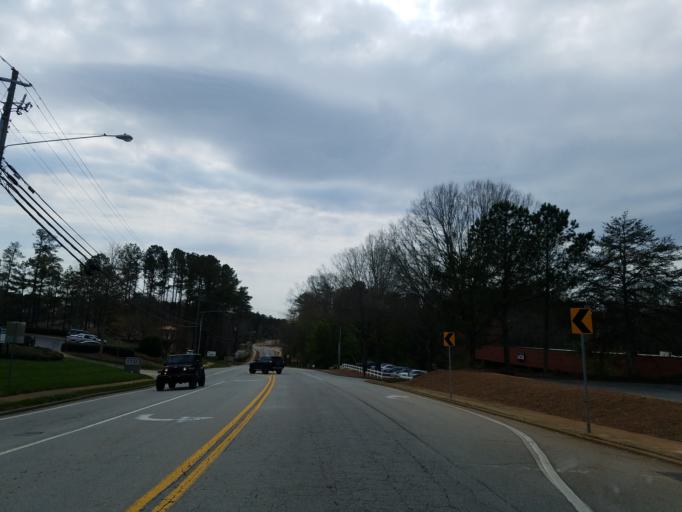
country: US
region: Georgia
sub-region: Fulton County
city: Alpharetta
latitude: 34.0551
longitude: -84.3143
